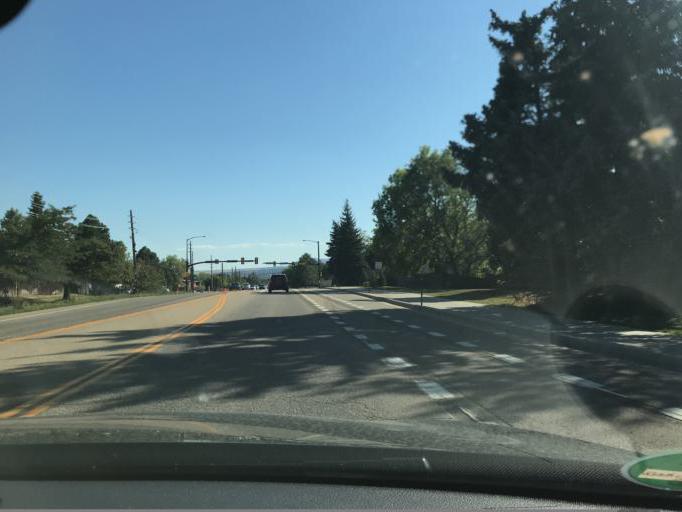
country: US
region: Colorado
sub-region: Boulder County
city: Boulder
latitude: 40.0448
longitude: -105.2586
